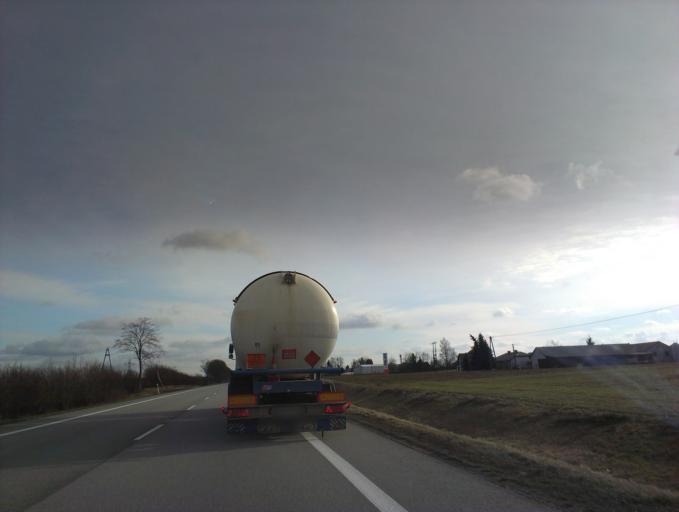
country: PL
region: Kujawsko-Pomorskie
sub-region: Powiat lipnowski
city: Kikol
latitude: 52.8840
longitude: 19.1356
